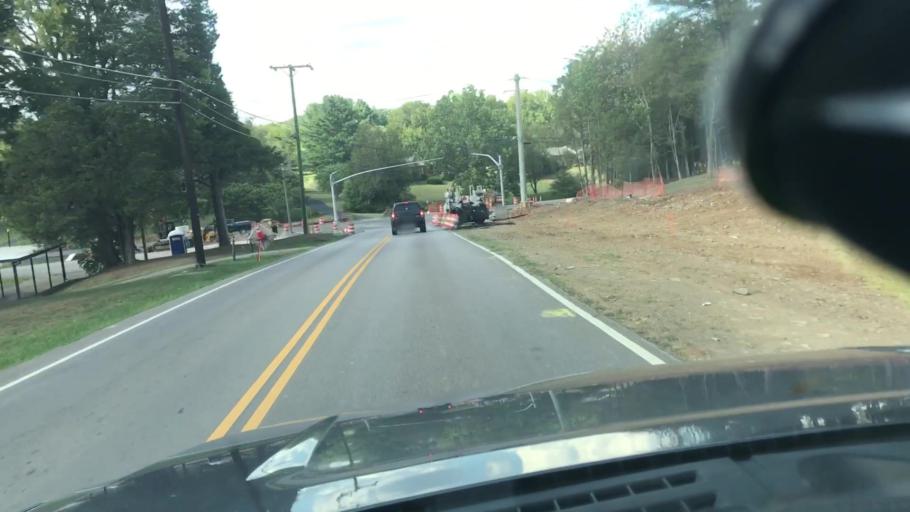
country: US
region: Tennessee
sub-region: Cheatham County
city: Pegram
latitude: 36.0345
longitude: -86.9681
